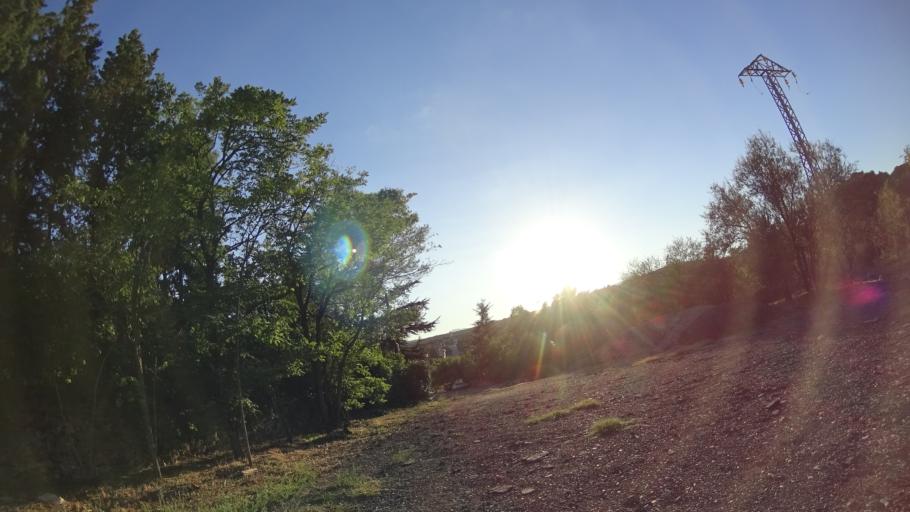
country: ES
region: Madrid
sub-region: Provincia de Madrid
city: Torrelodones
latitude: 40.5847
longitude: -3.9629
